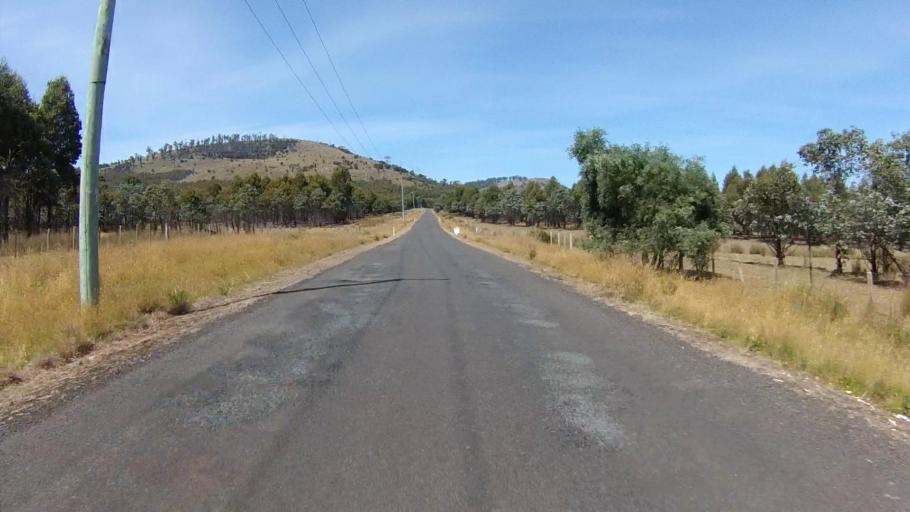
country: AU
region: Tasmania
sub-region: Sorell
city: Sorell
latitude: -42.6198
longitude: 147.7300
